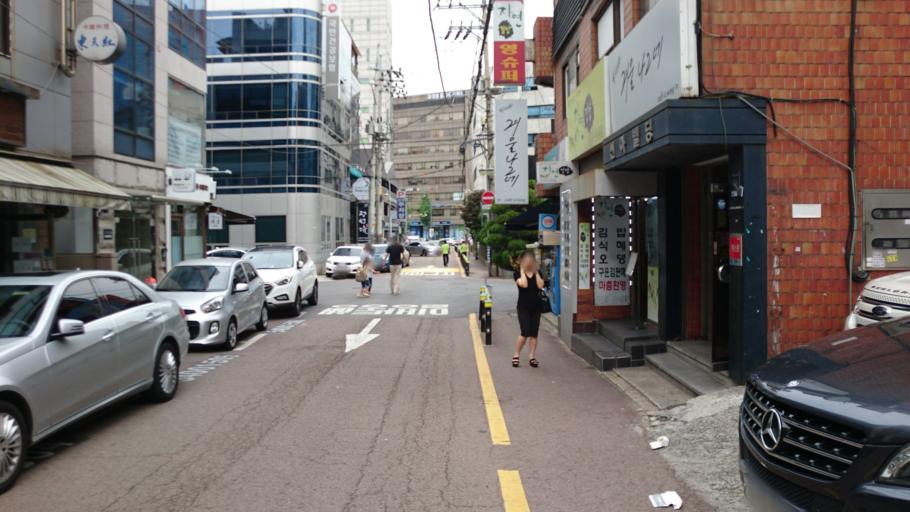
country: KR
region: Seoul
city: Seoul
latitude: 37.5281
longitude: 127.0323
